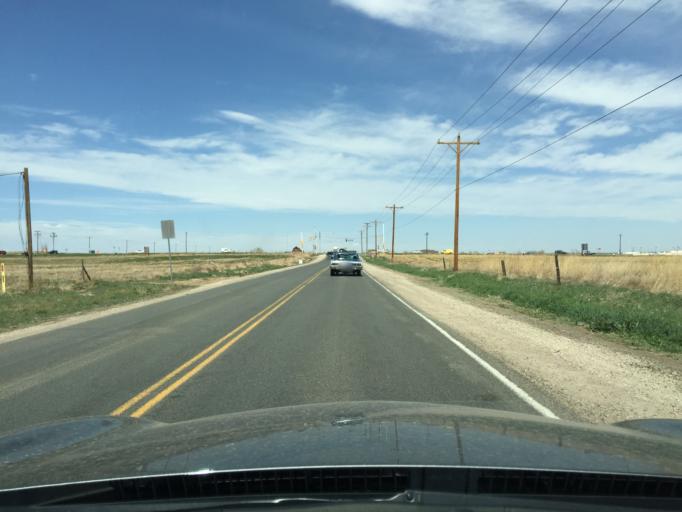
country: US
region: Colorado
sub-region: Boulder County
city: Erie
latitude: 39.9979
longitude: -104.9972
